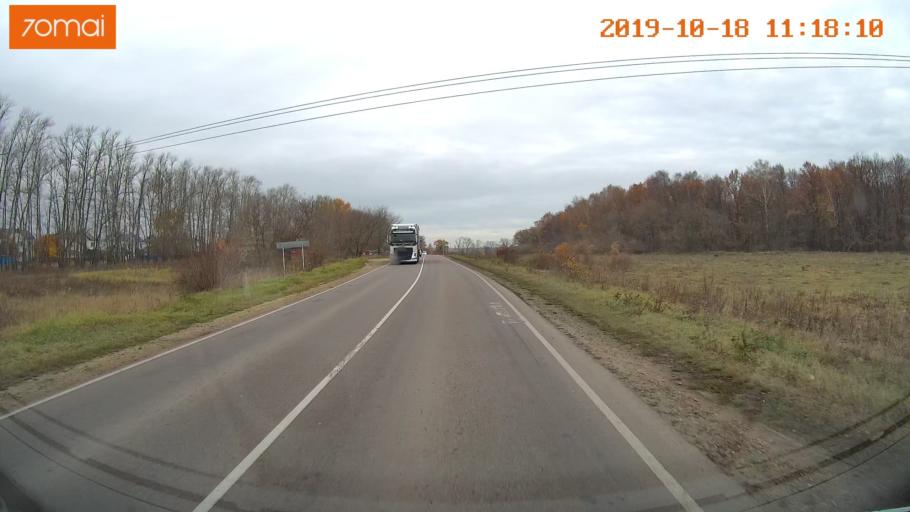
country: RU
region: Tula
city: Kimovsk
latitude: 54.0358
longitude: 38.5504
